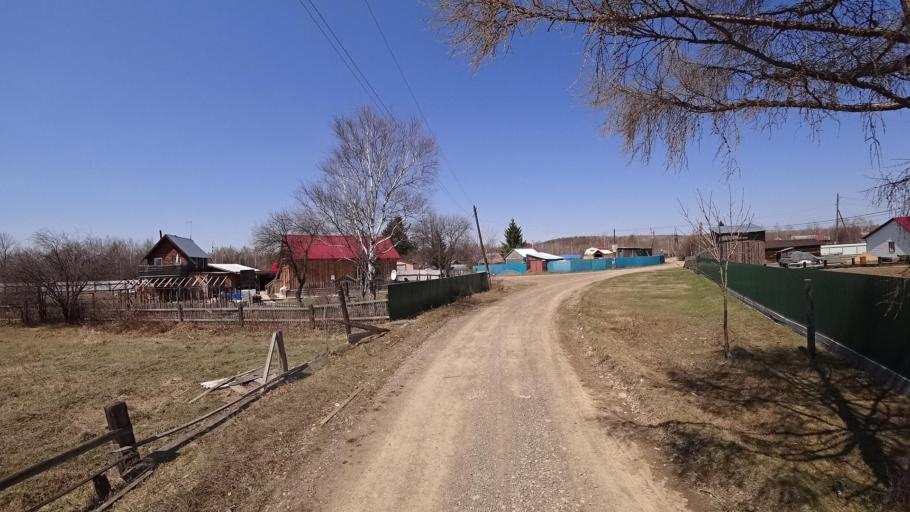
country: RU
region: Khabarovsk Krai
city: Khurba
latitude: 50.4109
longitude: 136.8626
